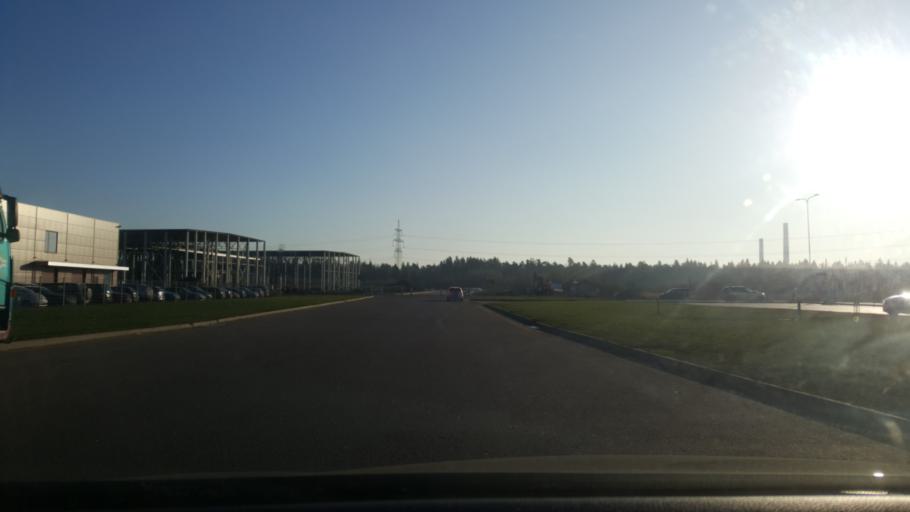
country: LT
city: Ramuciai
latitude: 54.9389
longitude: 24.0122
